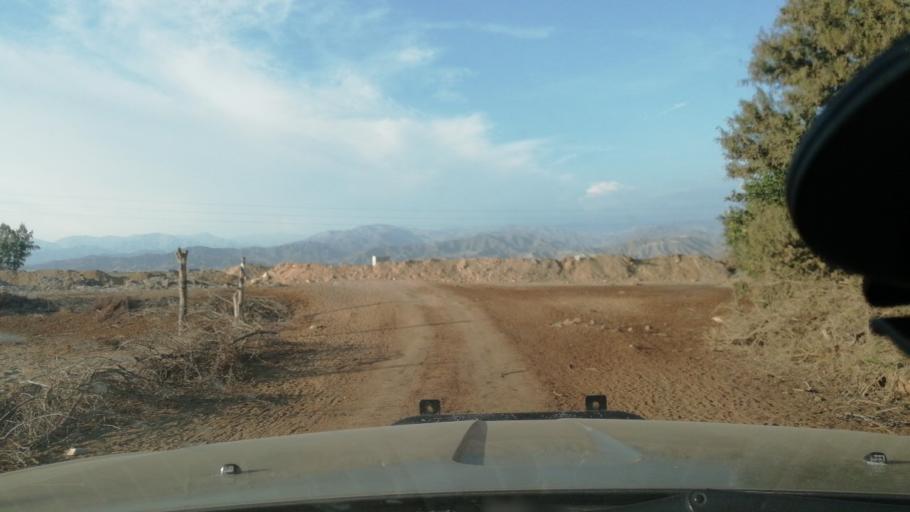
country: PE
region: Ica
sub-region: Provincia de Chincha
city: San Pedro
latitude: -13.3407
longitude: -76.1582
